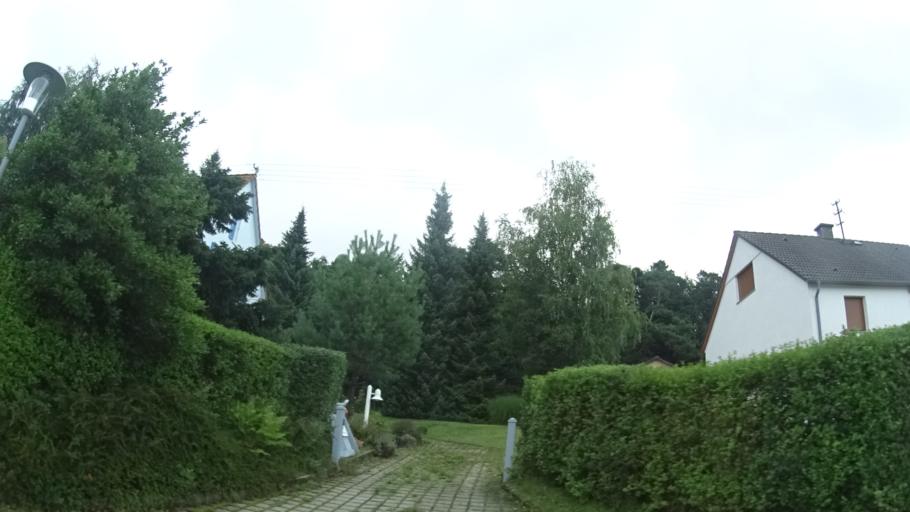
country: DE
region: Baden-Wuerttemberg
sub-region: Karlsruhe Region
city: Bad Herrenalb
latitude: 48.8200
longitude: 8.4612
